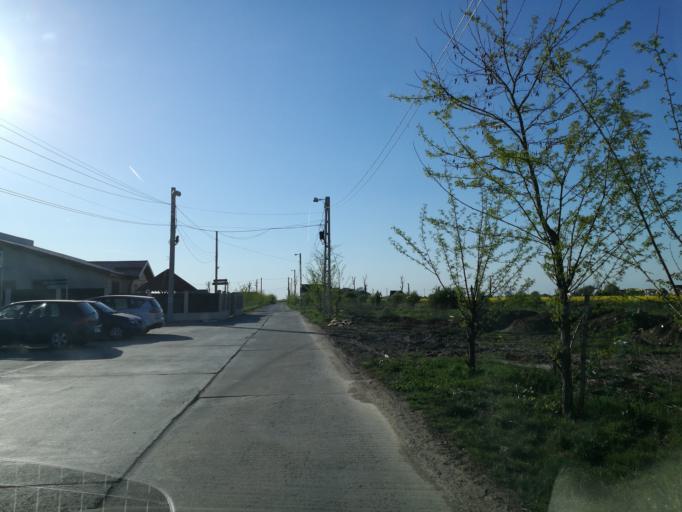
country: RO
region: Ilfov
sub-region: Comuna Vidra
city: Vidra
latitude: 44.2801
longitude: 26.1832
